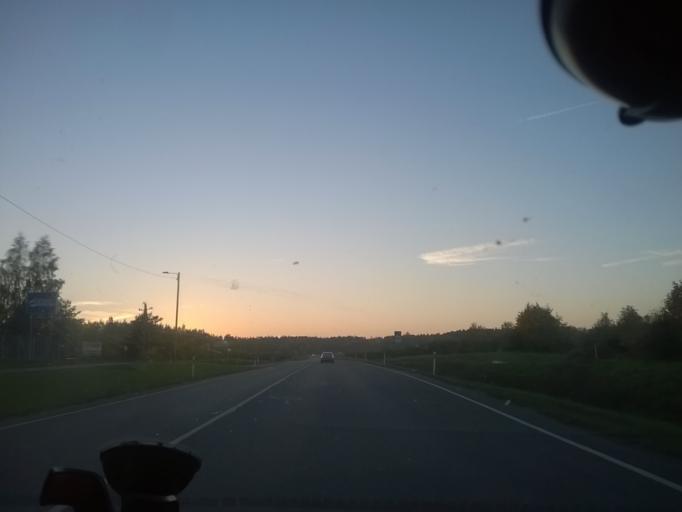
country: EE
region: Laeaene
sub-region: Ridala Parish
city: Uuemoisa
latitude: 58.9568
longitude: 23.7378
